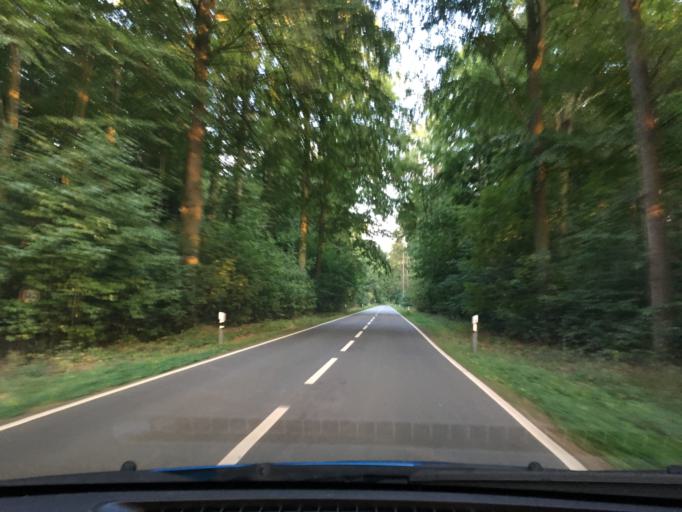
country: DE
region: Lower Saxony
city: Tosterglope
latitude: 53.2313
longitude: 10.7992
